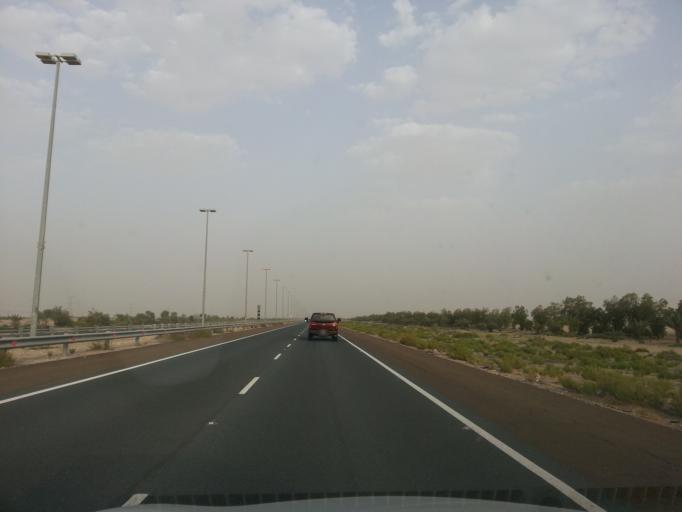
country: AE
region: Dubai
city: Dubai
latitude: 24.5952
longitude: 55.1387
